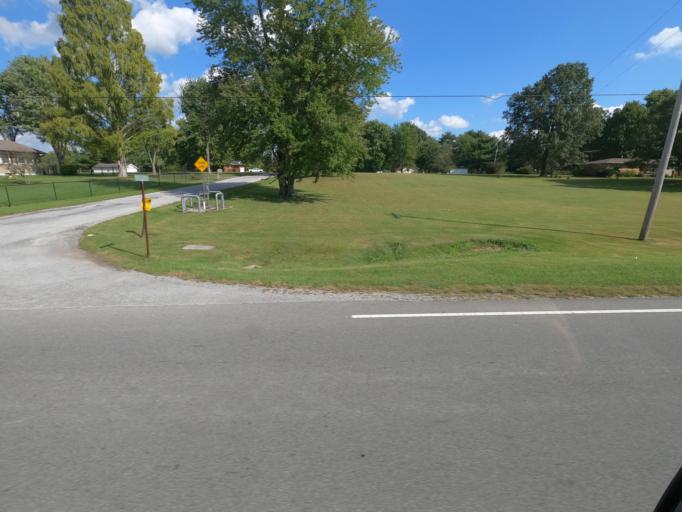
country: US
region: Illinois
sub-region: Massac County
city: Metropolis
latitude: 37.1694
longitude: -88.6766
